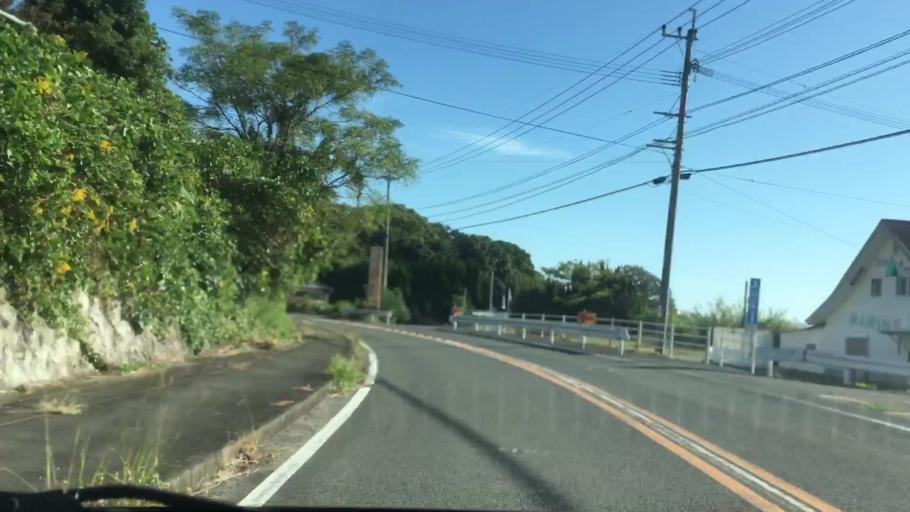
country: JP
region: Nagasaki
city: Sasebo
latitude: 33.0177
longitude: 129.7352
